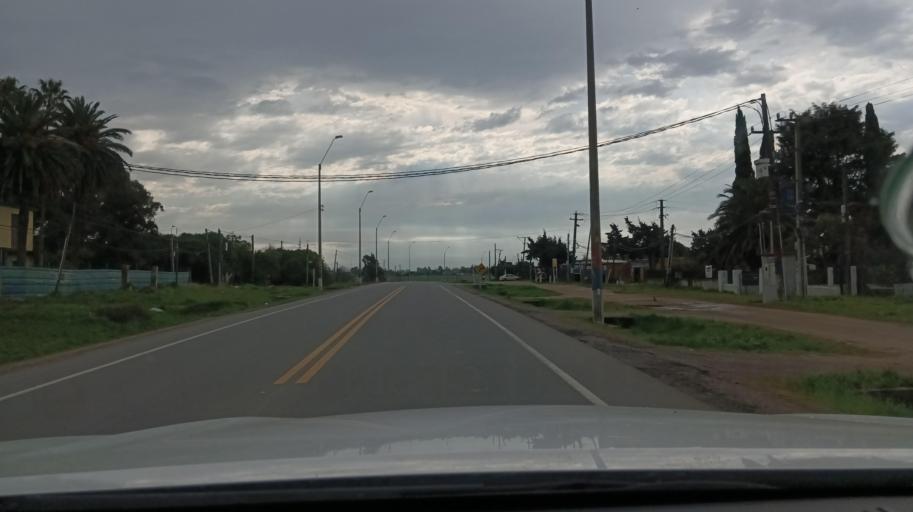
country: UY
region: Canelones
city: Toledo
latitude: -34.7474
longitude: -56.1108
